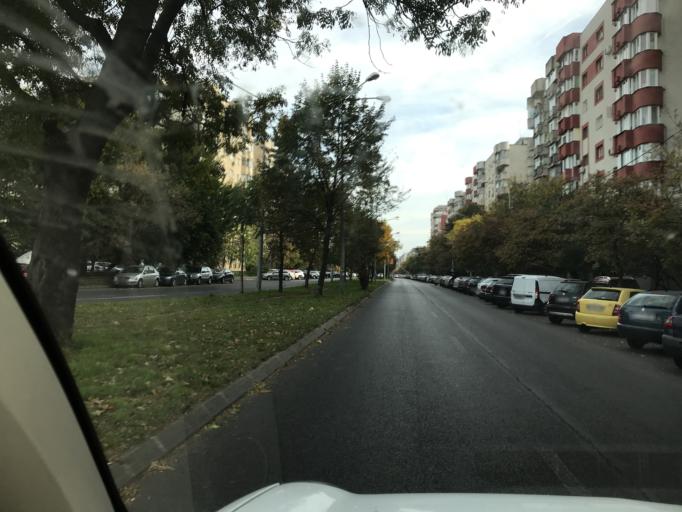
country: RO
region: Bucuresti
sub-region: Municipiul Bucuresti
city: Bucuresti
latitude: 44.4235
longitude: 26.0632
